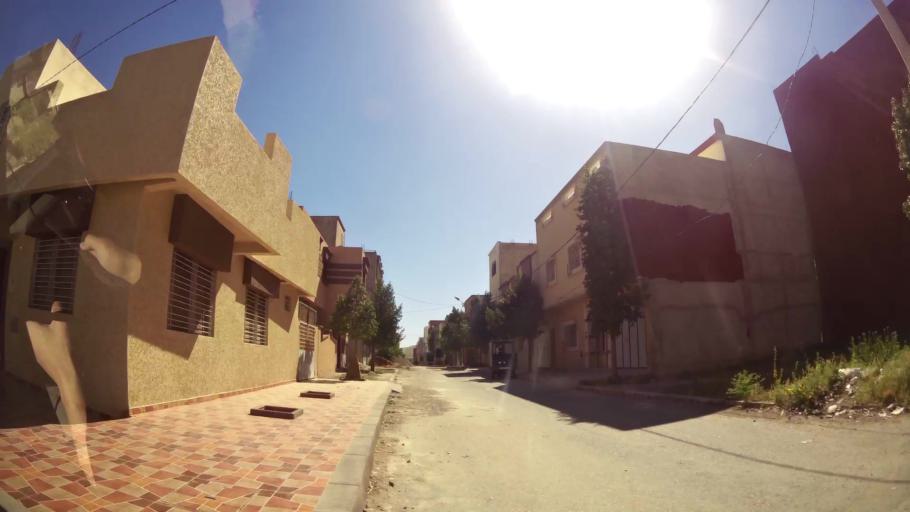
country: MA
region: Oriental
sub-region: Oujda-Angad
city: Oujda
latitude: 34.6511
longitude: -1.8856
